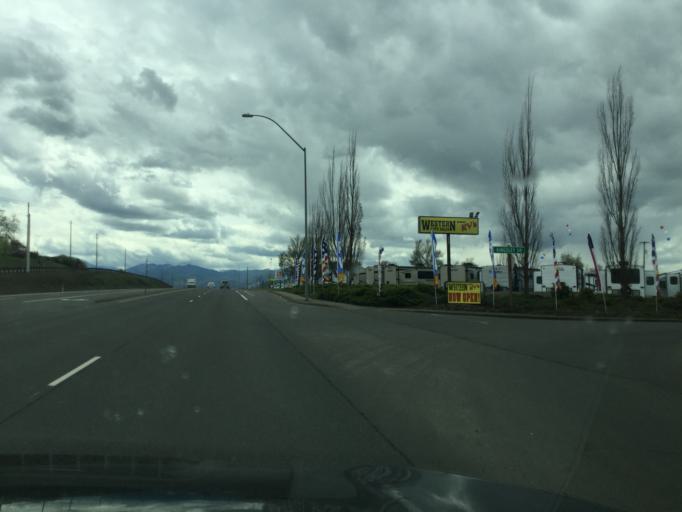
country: US
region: Oregon
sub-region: Jackson County
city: White City
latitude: 42.3855
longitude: -122.8560
